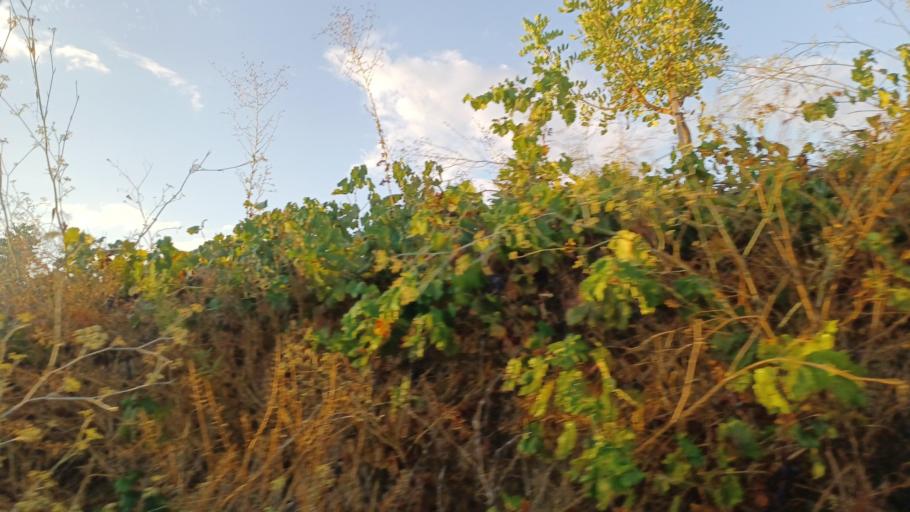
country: CY
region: Pafos
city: Tala
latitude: 34.9000
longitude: 32.4986
